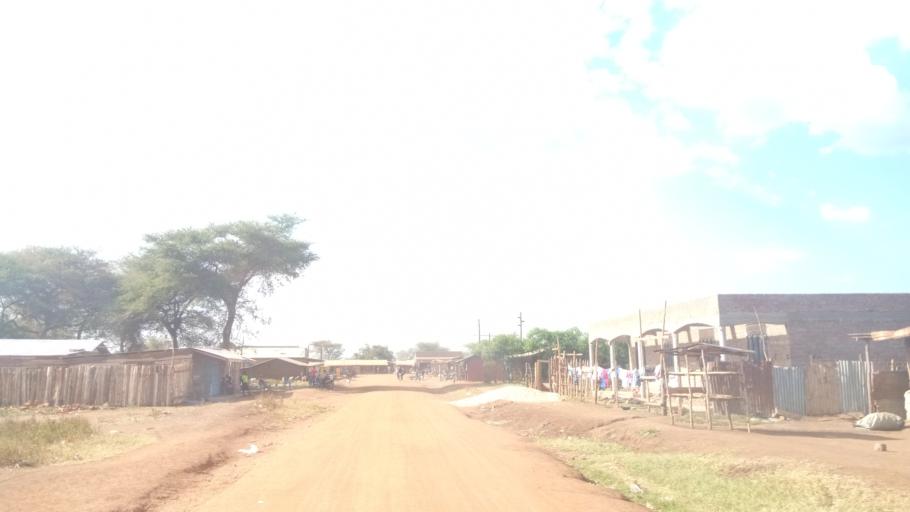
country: UG
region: Eastern Region
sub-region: Kween District
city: Binyin
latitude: 1.5246
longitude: 34.4901
